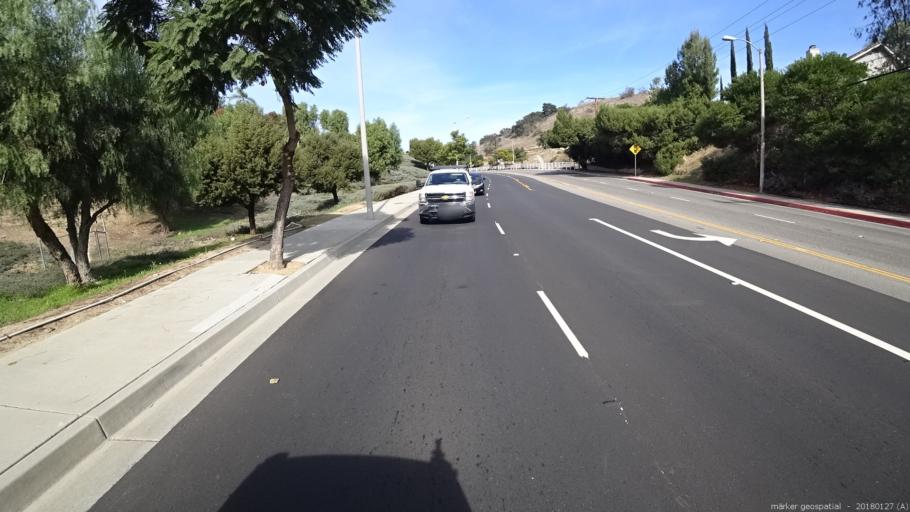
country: US
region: California
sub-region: Los Angeles County
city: Walnut
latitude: 33.9705
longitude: -117.8504
